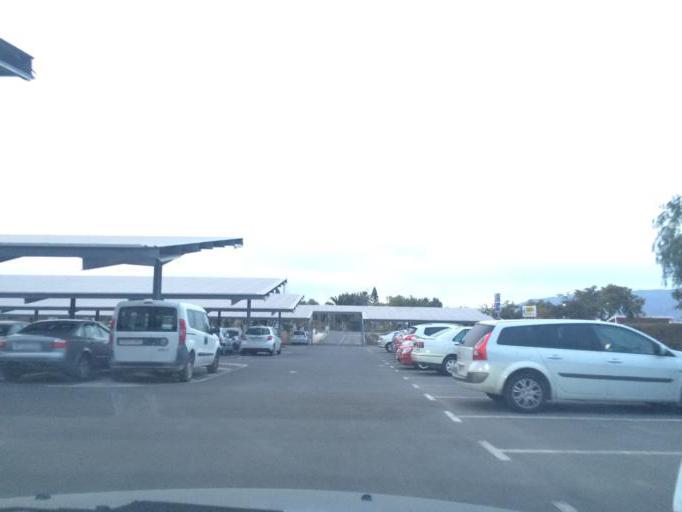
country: ES
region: Andalusia
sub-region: Provincia de Almeria
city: Almeria
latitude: 36.8319
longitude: -2.4014
